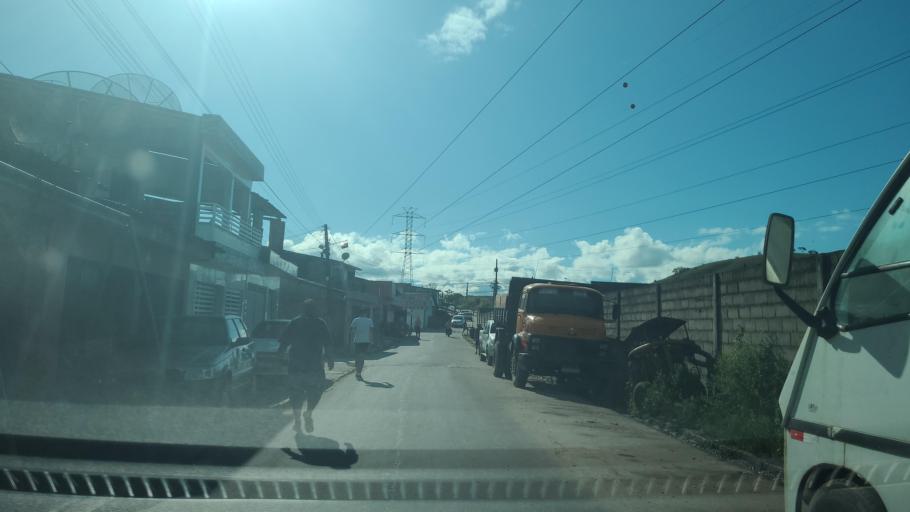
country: BR
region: Alagoas
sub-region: Uniao Dos Palmares
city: Uniao dos Palmares
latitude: -9.1548
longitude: -36.0227
